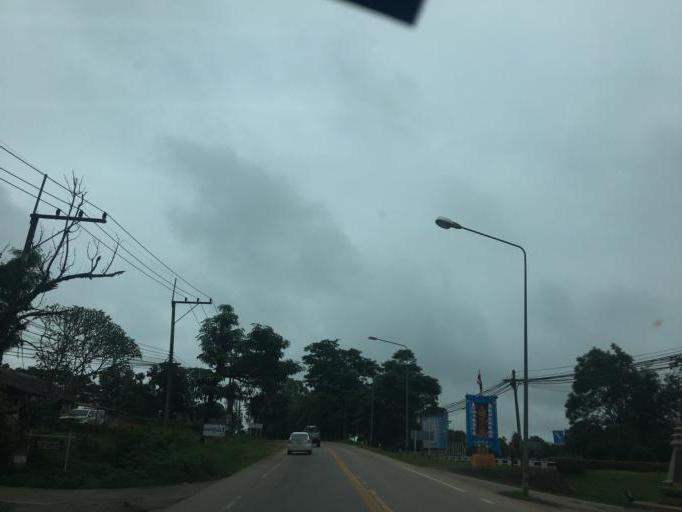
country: TH
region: Chiang Rai
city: Chiang Rai
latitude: 20.0034
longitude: 99.8708
